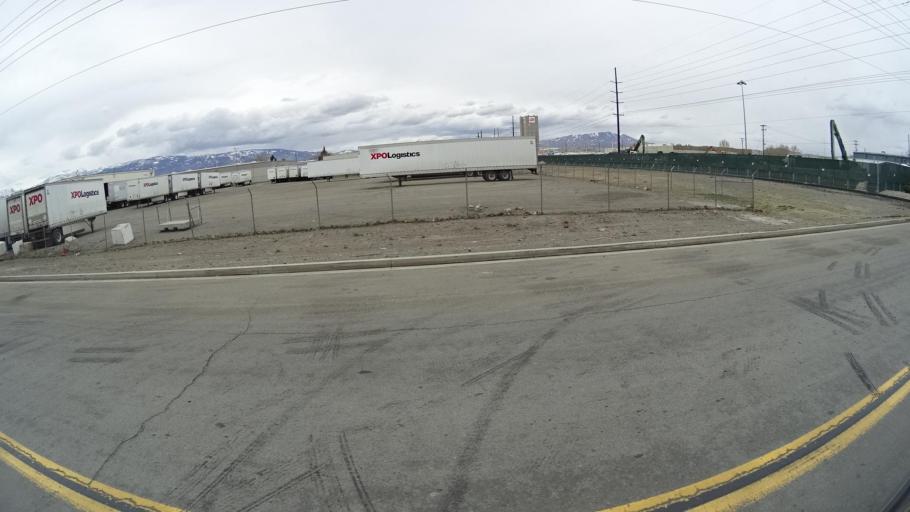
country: US
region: Nevada
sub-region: Washoe County
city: Sparks
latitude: 39.5189
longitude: -119.7198
